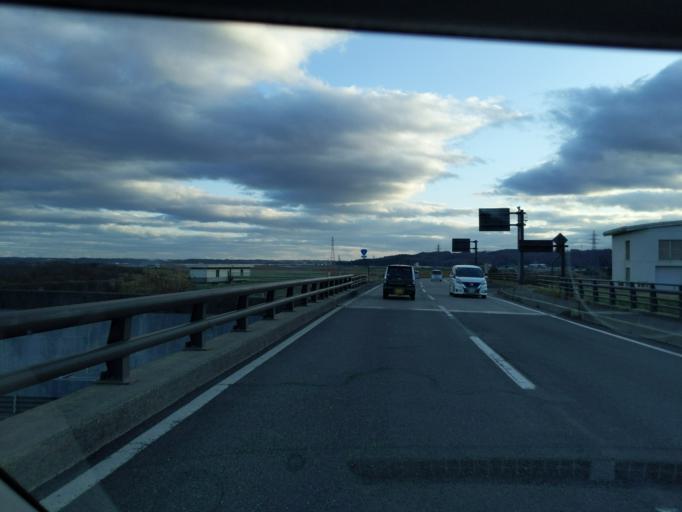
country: JP
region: Iwate
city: Ichinoseki
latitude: 38.9862
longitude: 141.1238
